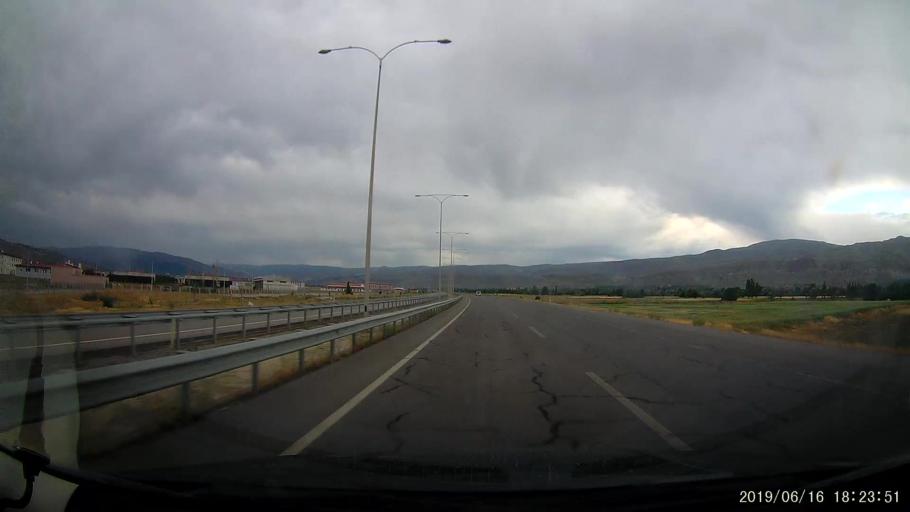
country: TR
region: Erzincan
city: Erzincan
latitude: 39.7546
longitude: 39.4129
